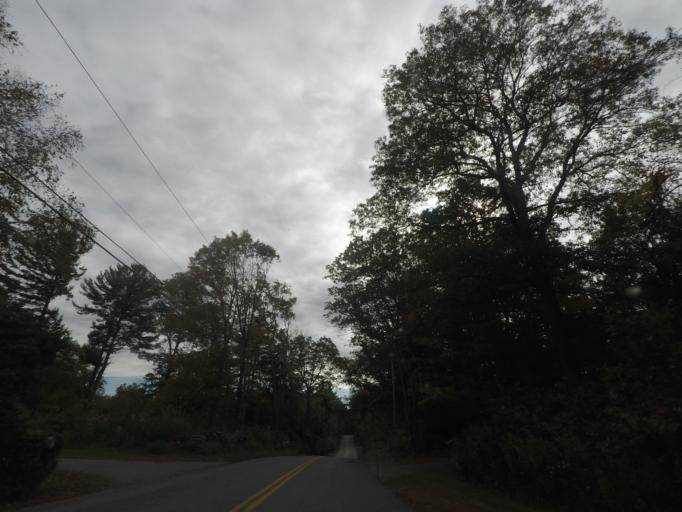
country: US
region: Connecticut
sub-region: Windham County
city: Thompson
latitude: 41.9494
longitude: -71.8409
